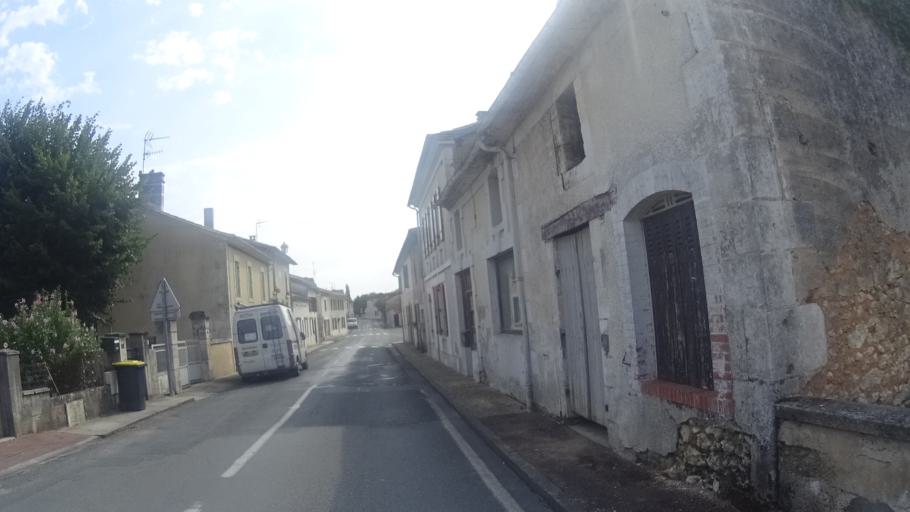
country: FR
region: Aquitaine
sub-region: Departement de la Dordogne
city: Mussidan
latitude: 45.0542
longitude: 0.3635
